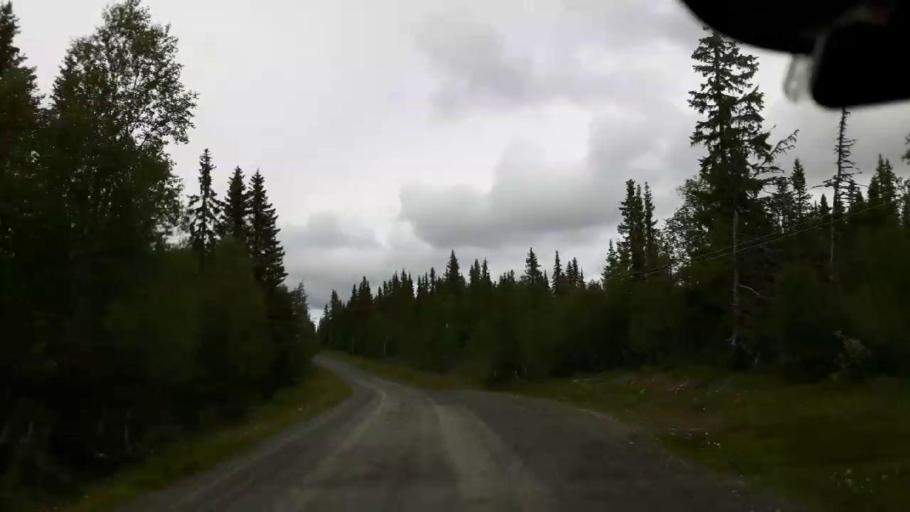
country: SE
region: Jaemtland
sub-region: Krokoms Kommun
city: Valla
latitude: 63.7388
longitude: 13.8379
